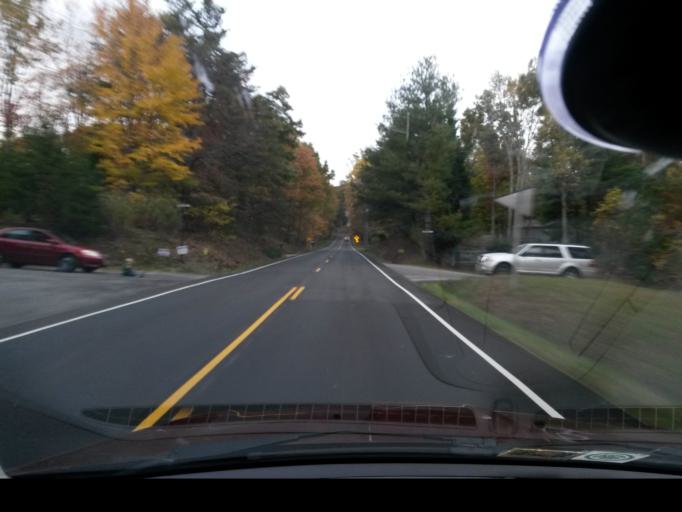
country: US
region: Virginia
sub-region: Roanoke County
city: Narrows
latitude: 37.1974
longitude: -79.8842
